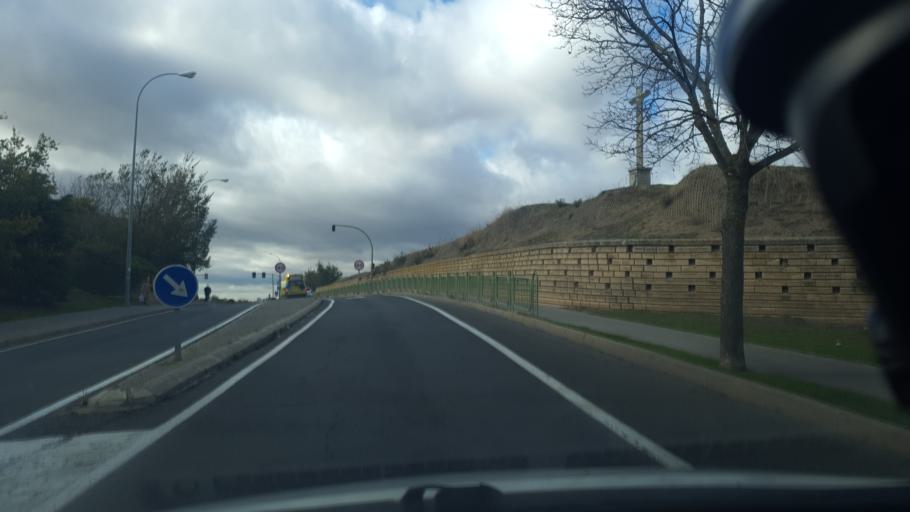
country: ES
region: Castille and Leon
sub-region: Provincia de Segovia
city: Segovia
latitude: 40.9442
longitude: -4.1250
